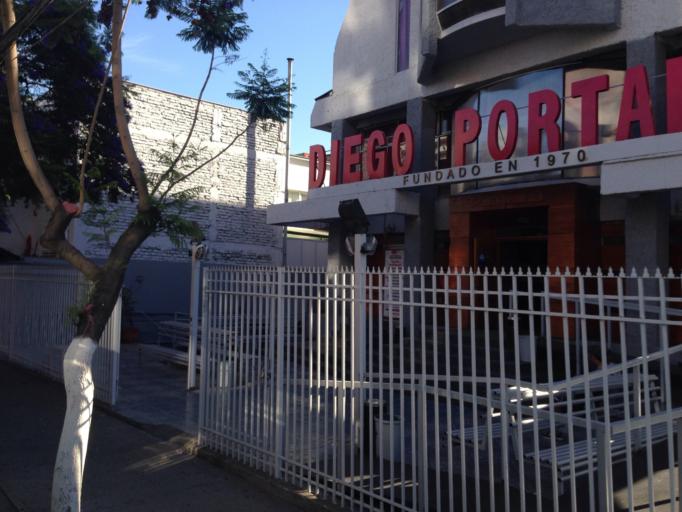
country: CL
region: Santiago Metropolitan
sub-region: Provincia de Santiago
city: Santiago
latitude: -33.4507
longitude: -70.6213
